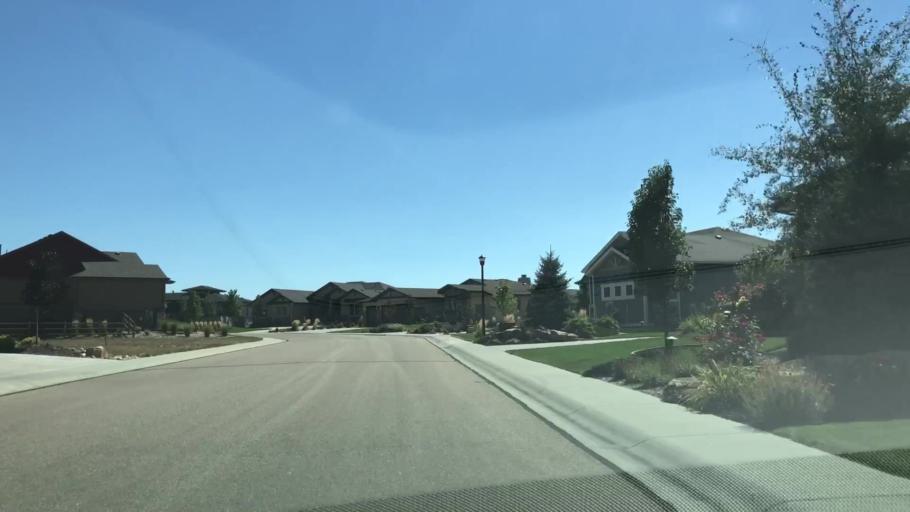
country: US
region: Colorado
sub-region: Weld County
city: Windsor
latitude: 40.4526
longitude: -104.9619
